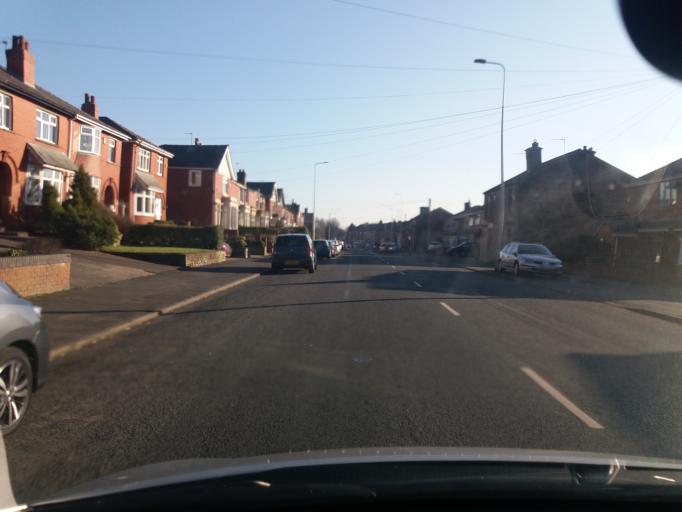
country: GB
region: England
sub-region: Lancashire
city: Adlington
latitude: 53.6239
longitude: -2.6066
